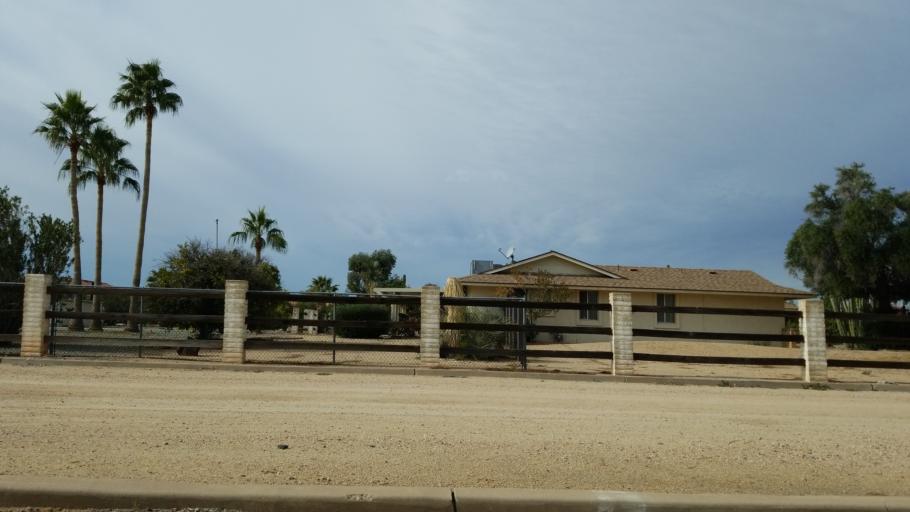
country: US
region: Arizona
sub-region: Maricopa County
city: Youngtown
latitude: 33.5782
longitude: -112.2988
